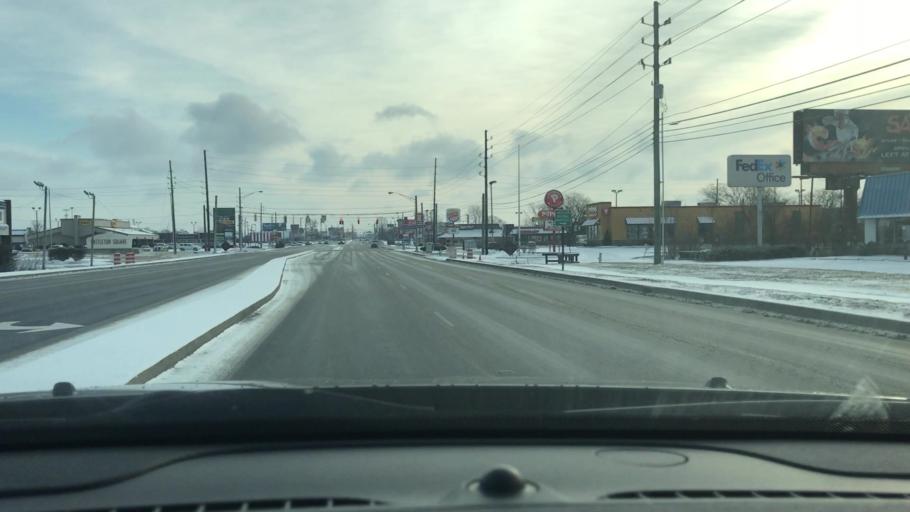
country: US
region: Indiana
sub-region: Hamilton County
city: Fishers
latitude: 39.9053
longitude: -86.0621
